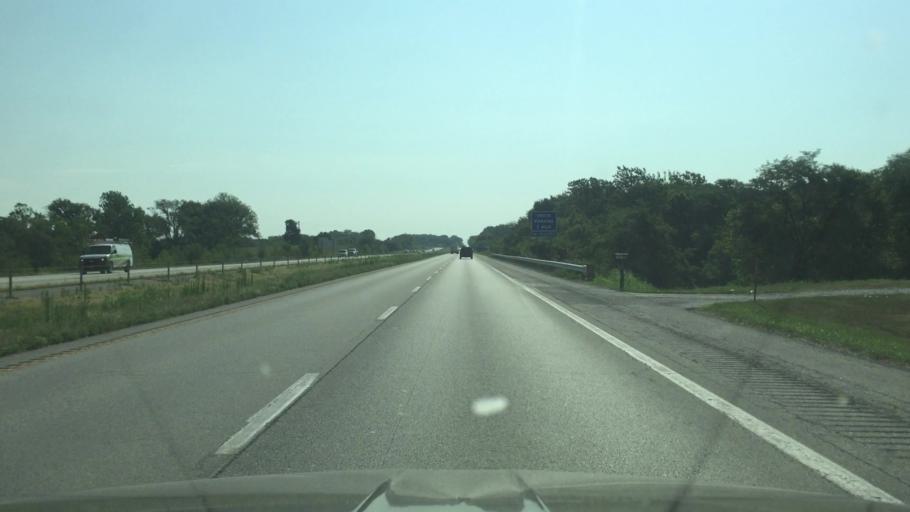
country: US
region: Missouri
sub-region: Jackson County
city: Lone Jack
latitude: 38.8692
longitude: -94.1664
